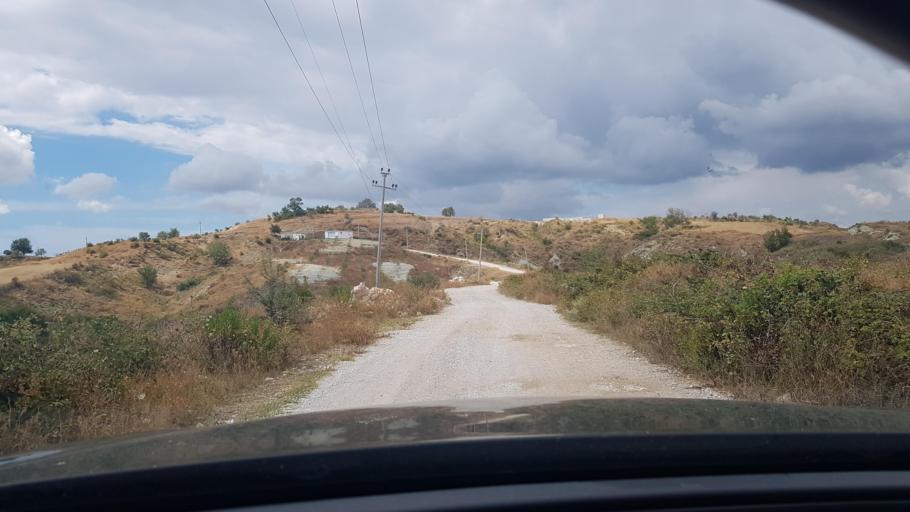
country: AL
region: Tirane
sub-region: Rrethi i Kavajes
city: Golem
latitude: 41.2912
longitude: 19.5479
